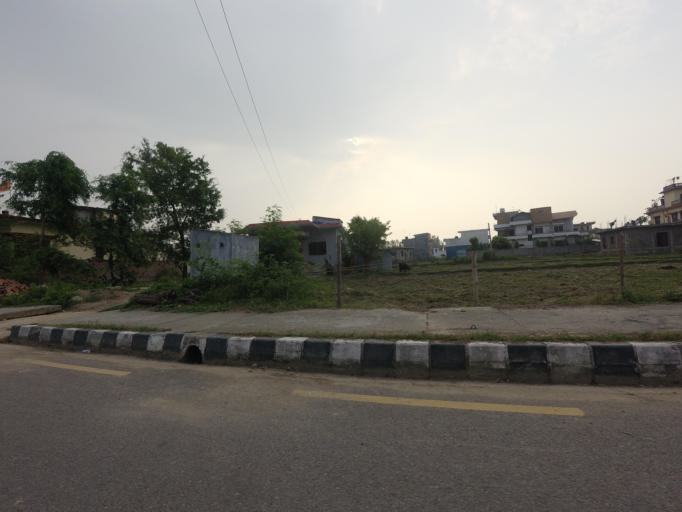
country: NP
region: Western Region
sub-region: Lumbini Zone
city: Bhairahawa
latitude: 27.4997
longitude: 83.4441
